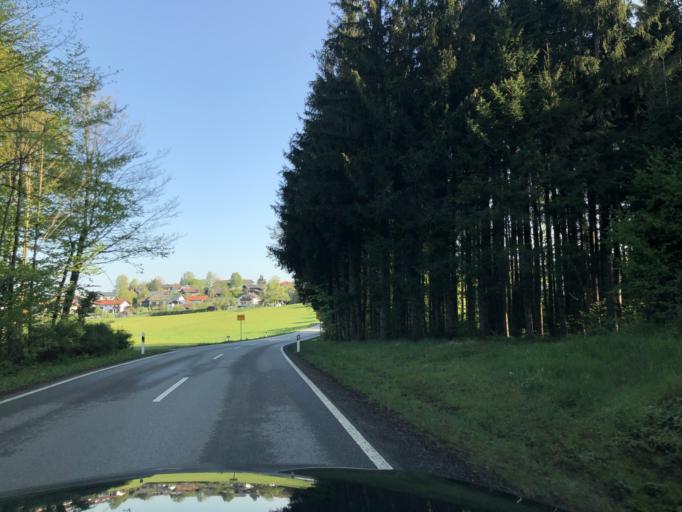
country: DE
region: Bavaria
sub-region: Upper Bavaria
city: Frasdorf
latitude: 47.8249
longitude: 12.2575
